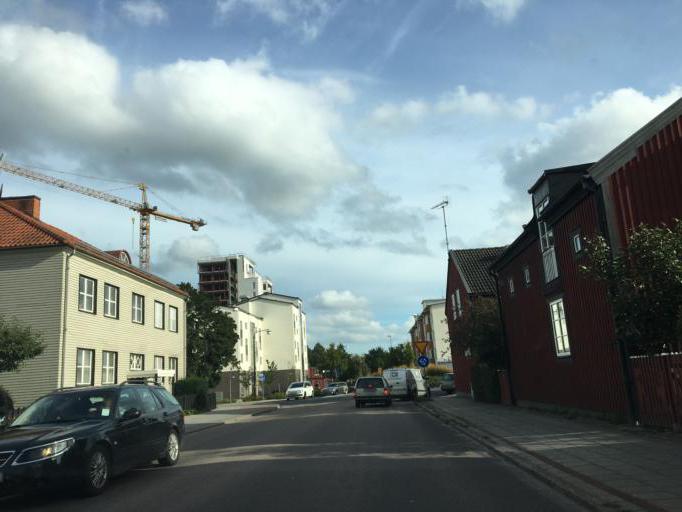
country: SE
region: Uppsala
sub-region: Enkopings Kommun
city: Enkoping
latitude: 59.6358
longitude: 17.0841
